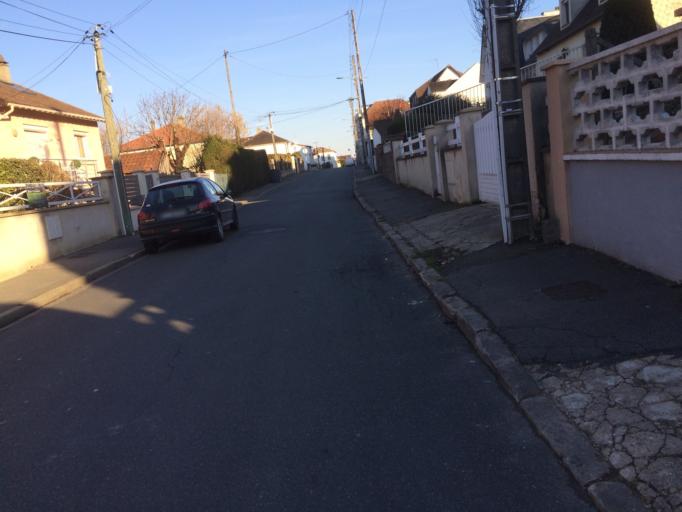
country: FR
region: Ile-de-France
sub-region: Departement de l'Essonne
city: Igny
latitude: 48.7332
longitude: 2.2188
